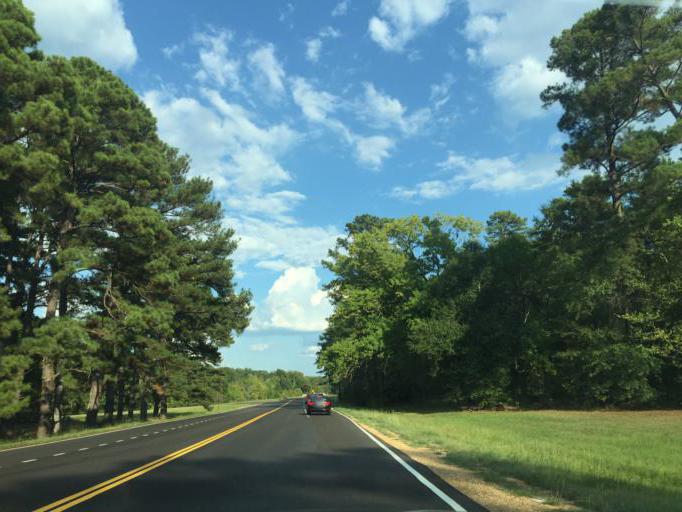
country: US
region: Mississippi
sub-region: Madison County
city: Ridgeland
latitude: 32.4274
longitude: -90.1118
